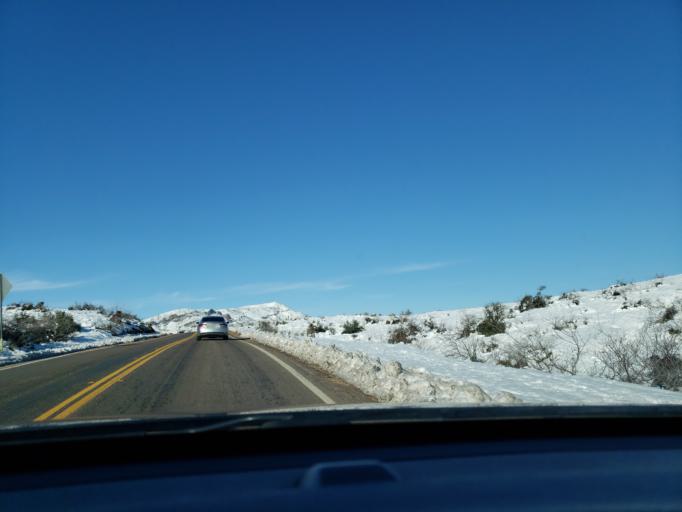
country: US
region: Arizona
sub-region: Maricopa County
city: Carefree
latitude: 33.8717
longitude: -111.8231
